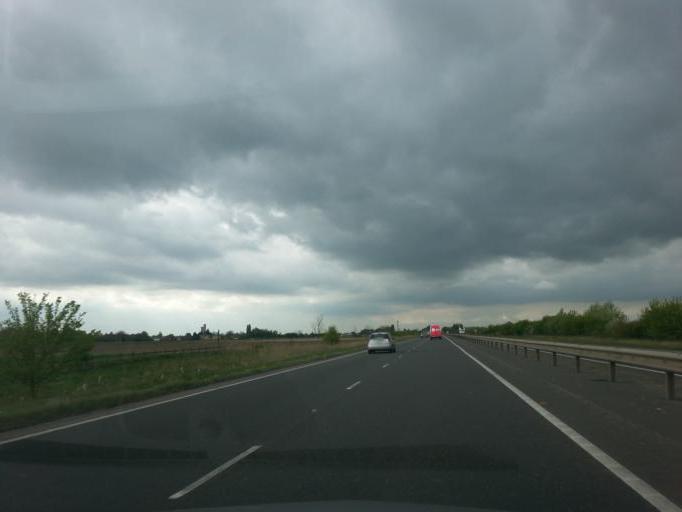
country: GB
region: England
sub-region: Peterborough
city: Thorney
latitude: 52.6252
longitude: -0.0916
